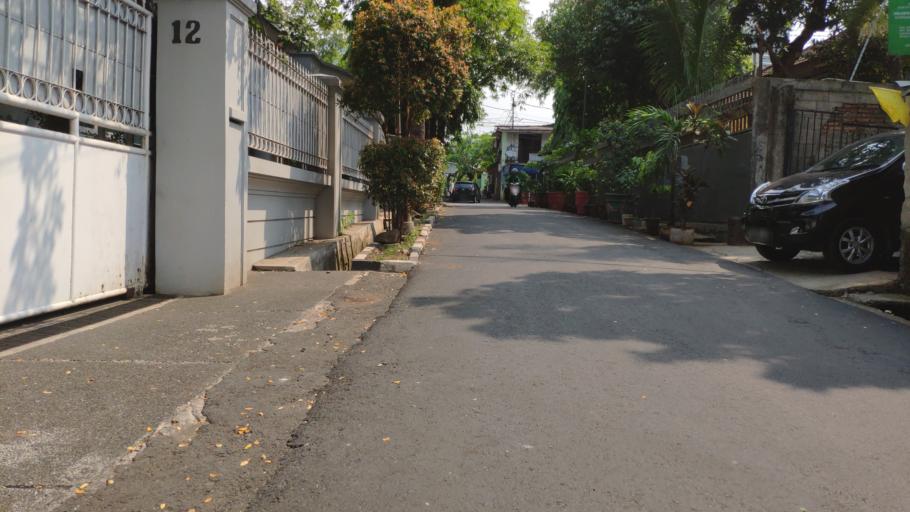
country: ID
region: Jakarta Raya
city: Jakarta
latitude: -6.2523
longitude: 106.8120
